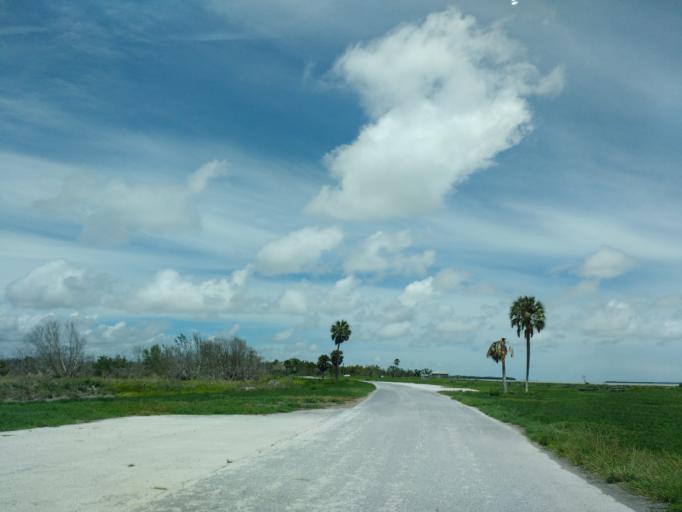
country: US
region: Florida
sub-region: Monroe County
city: Islamorada
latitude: 25.1373
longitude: -80.9366
